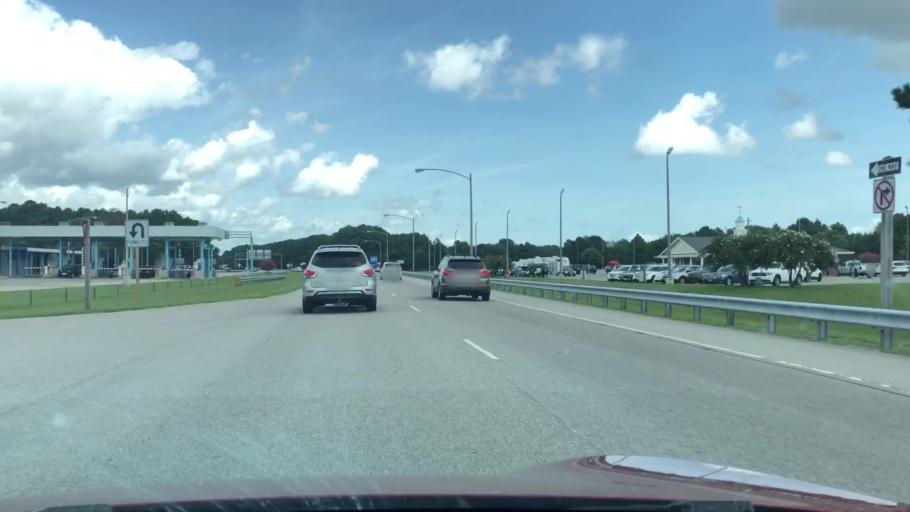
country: US
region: Virginia
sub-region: Northampton County
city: Cape Charles
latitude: 37.1320
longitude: -75.9662
